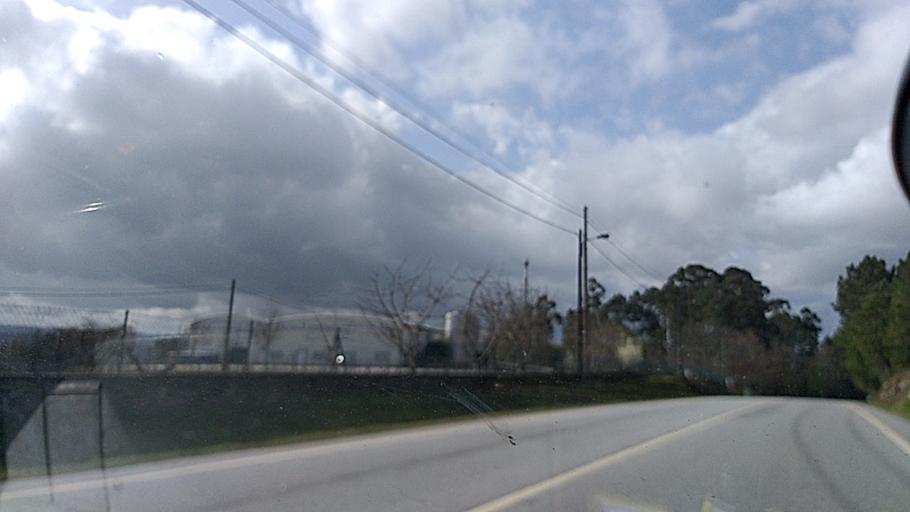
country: PT
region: Viseu
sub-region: Mangualde
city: Mangualde
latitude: 40.6598
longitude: -7.7211
